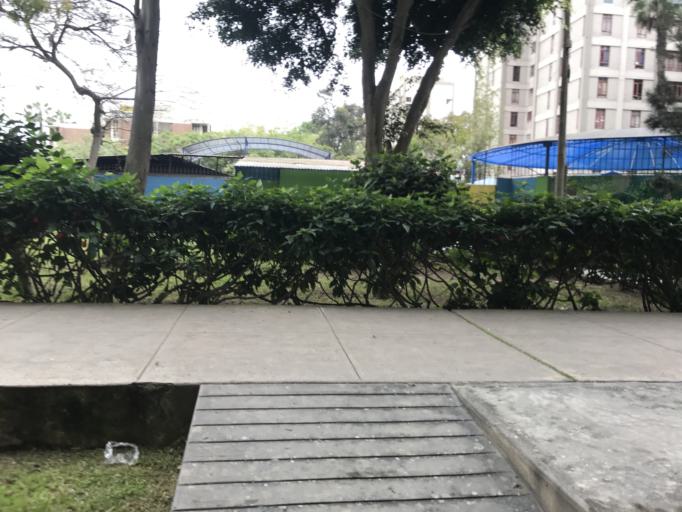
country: PE
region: Lima
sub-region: Lima
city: San Isidro
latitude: -12.0886
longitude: -77.0535
